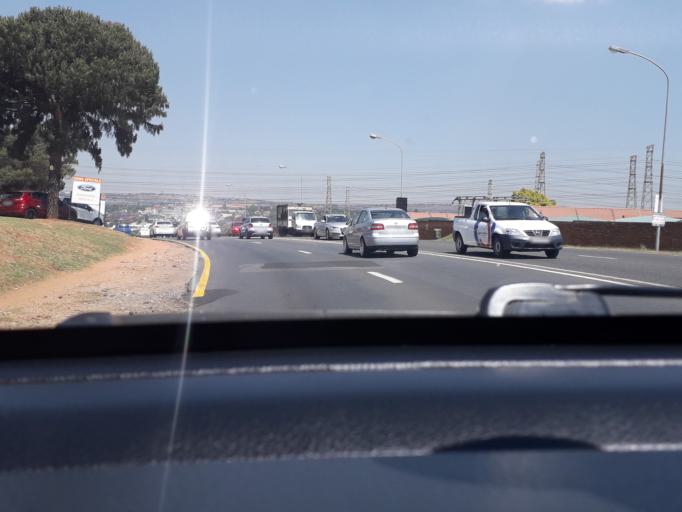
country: ZA
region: Gauteng
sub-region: City of Johannesburg Metropolitan Municipality
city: Modderfontein
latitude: -26.1231
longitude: 28.1399
